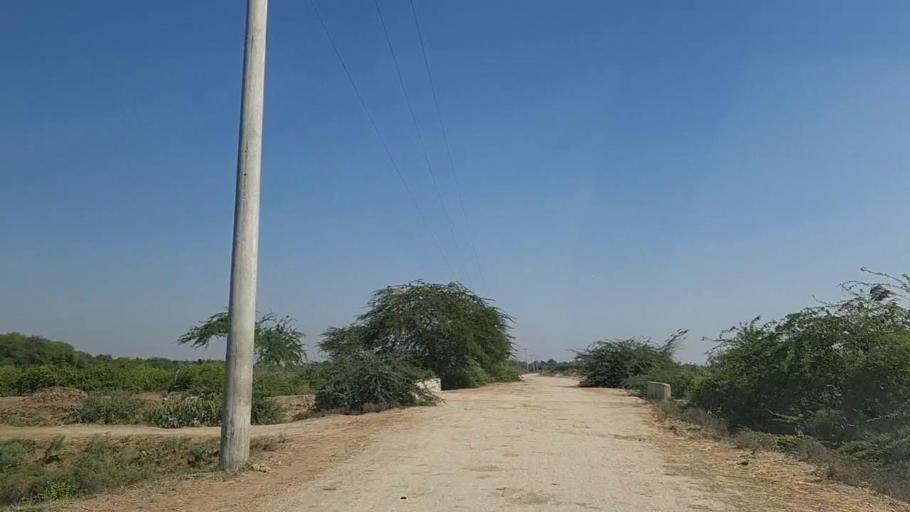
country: PK
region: Sindh
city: Daro Mehar
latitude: 24.7211
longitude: 68.1737
